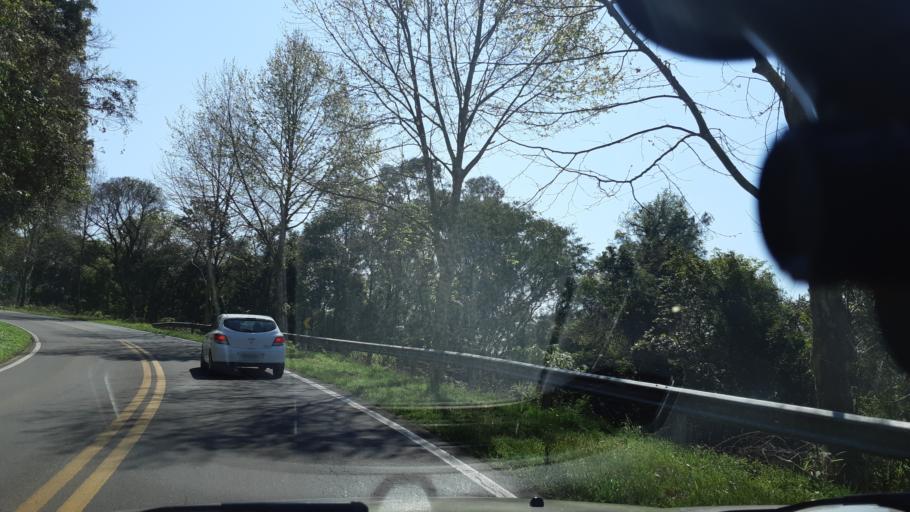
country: BR
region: Rio Grande do Sul
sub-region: Nova Petropolis
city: Nova Petropolis
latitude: -29.4044
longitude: -51.1242
